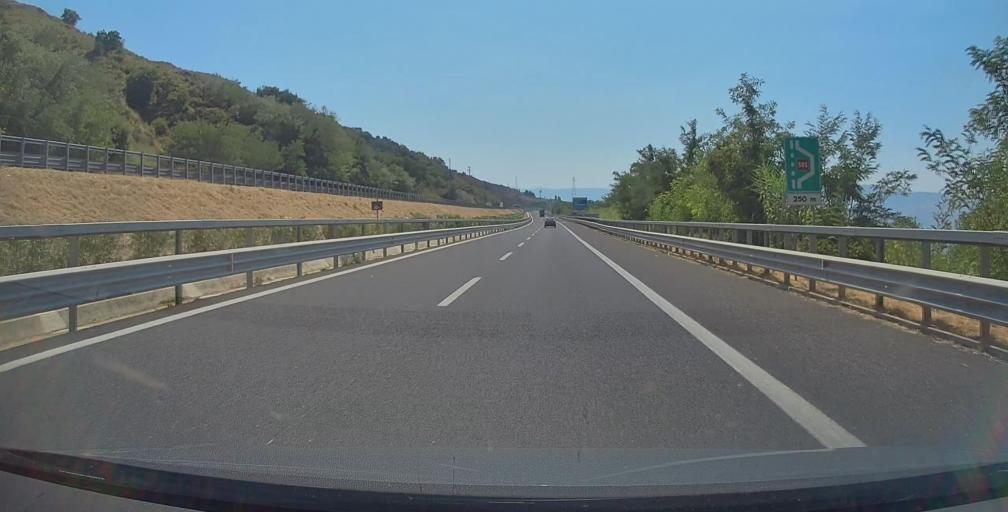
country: IT
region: Calabria
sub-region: Provincia di Reggio Calabria
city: Villa San Giovanni
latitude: 38.2311
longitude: 15.6620
